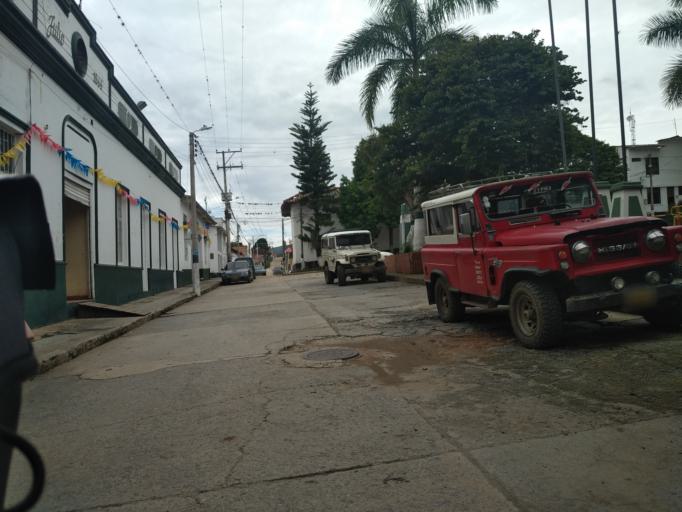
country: CO
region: Santander
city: Guepsa
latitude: 6.0252
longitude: -73.5722
